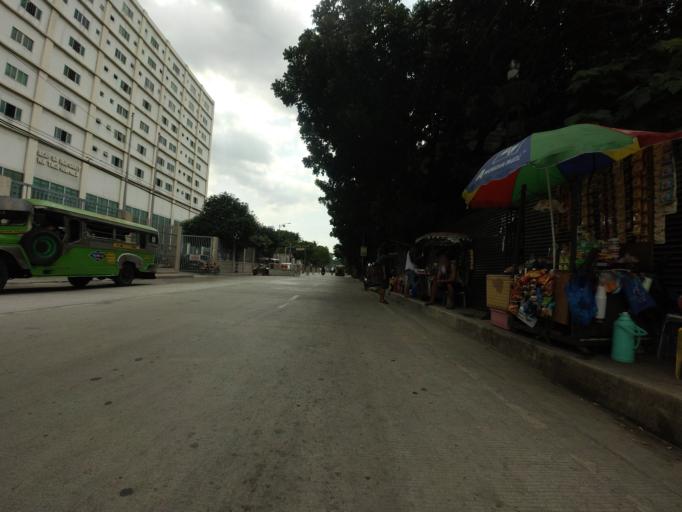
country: PH
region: Metro Manila
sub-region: San Juan
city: San Juan
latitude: 14.5837
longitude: 121.0162
